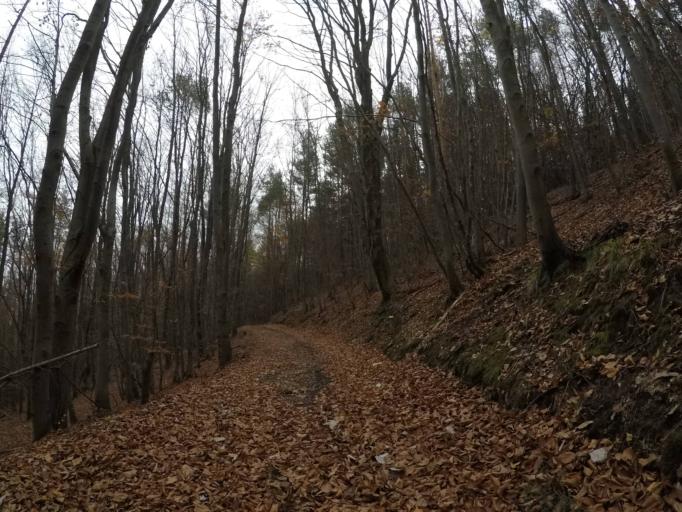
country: SK
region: Presovsky
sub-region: Okres Presov
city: Presov
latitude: 48.8987
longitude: 21.1687
